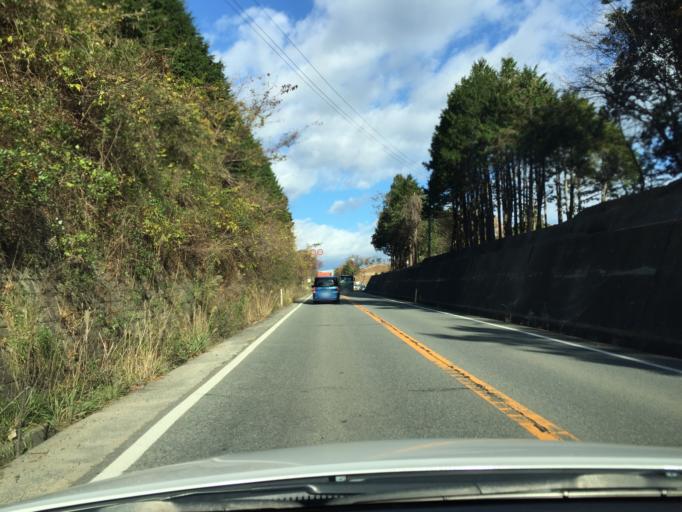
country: JP
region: Fukushima
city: Namie
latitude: 37.3479
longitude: 141.0116
